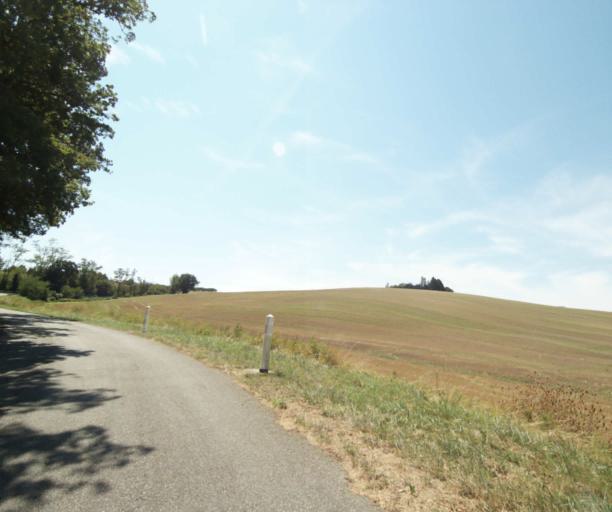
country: FR
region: Midi-Pyrenees
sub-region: Departement de l'Ariege
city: Lezat-sur-Leze
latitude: 43.2609
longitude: 1.3216
